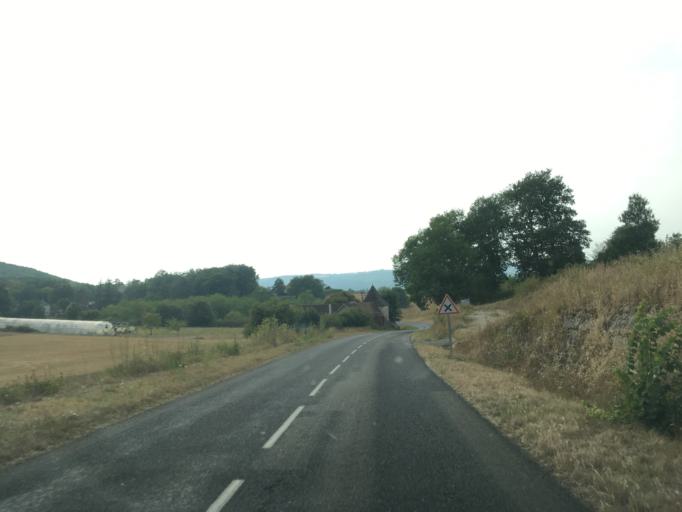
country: FR
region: Midi-Pyrenees
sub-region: Departement du Lot
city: Souillac
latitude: 44.8498
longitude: 1.5386
